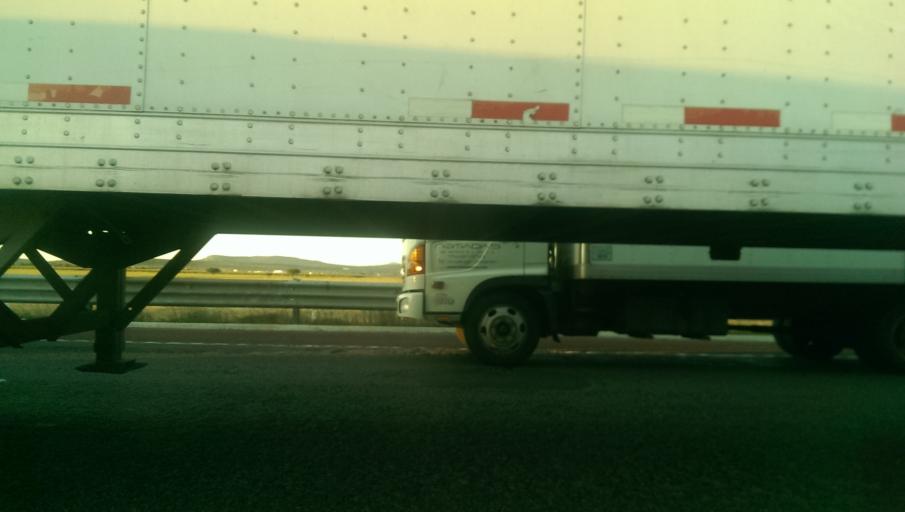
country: MX
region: Queretaro
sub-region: San Juan del Rio
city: El Cazadero
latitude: 20.2797
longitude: -99.8992
